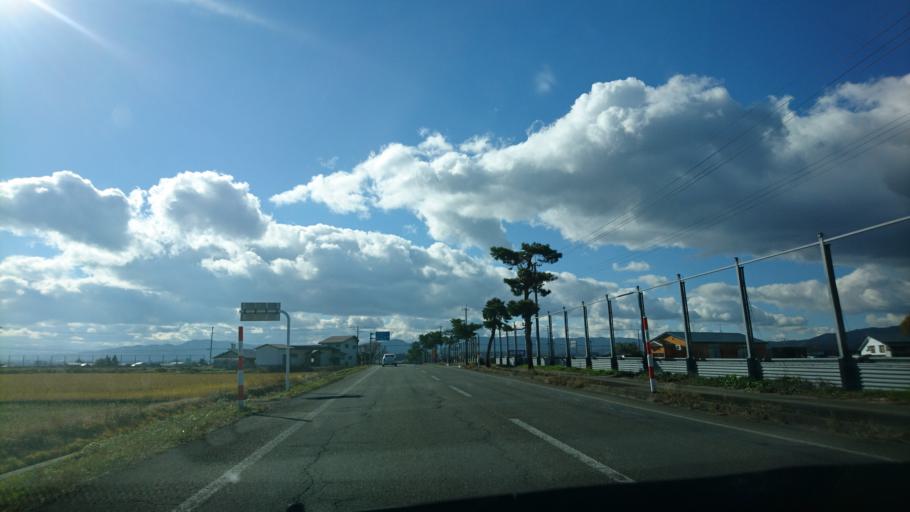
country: JP
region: Akita
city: Yokotemachi
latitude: 39.2763
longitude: 140.4320
